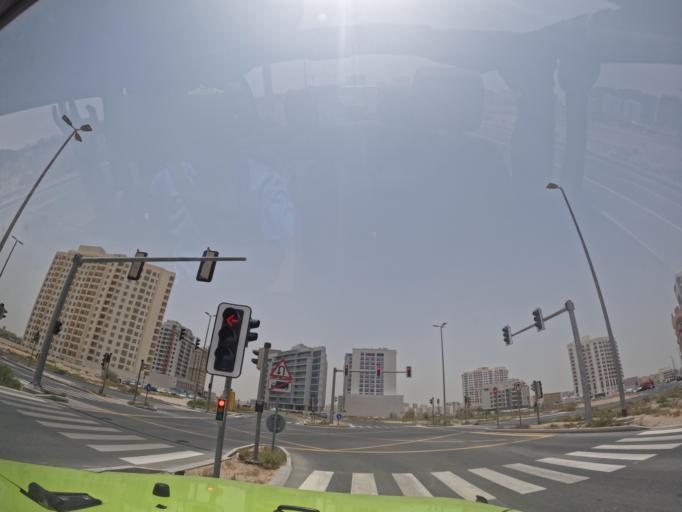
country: AE
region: Dubai
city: Dubai
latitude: 25.0947
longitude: 55.3746
